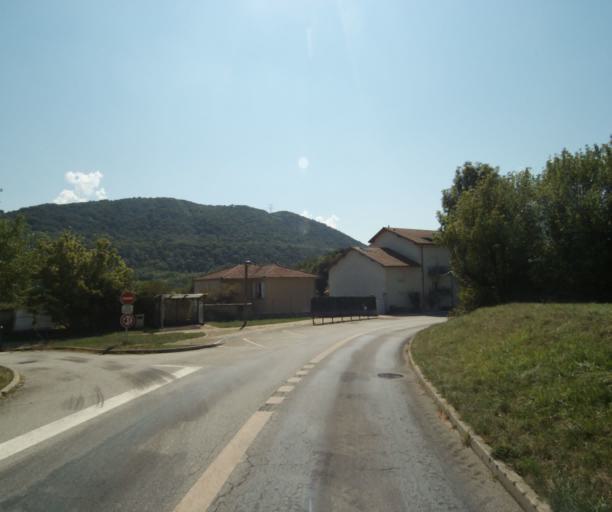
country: FR
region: Rhone-Alpes
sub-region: Departement de l'Isere
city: Champagnier
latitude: 45.1008
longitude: 5.7422
